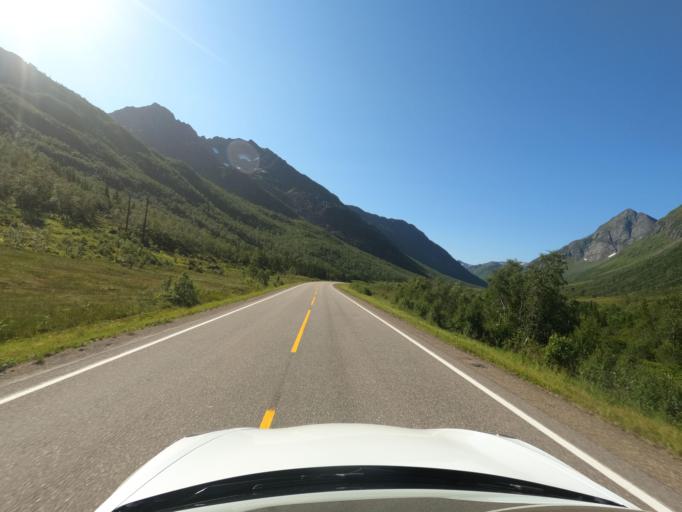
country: NO
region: Nordland
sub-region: Lodingen
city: Lodingen
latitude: 68.5215
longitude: 15.7556
